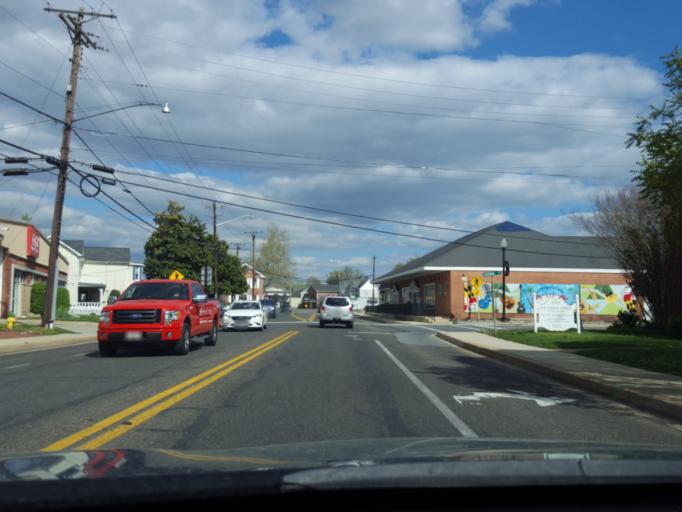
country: US
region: Maryland
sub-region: Charles County
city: La Plata
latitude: 38.5295
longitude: -76.9774
